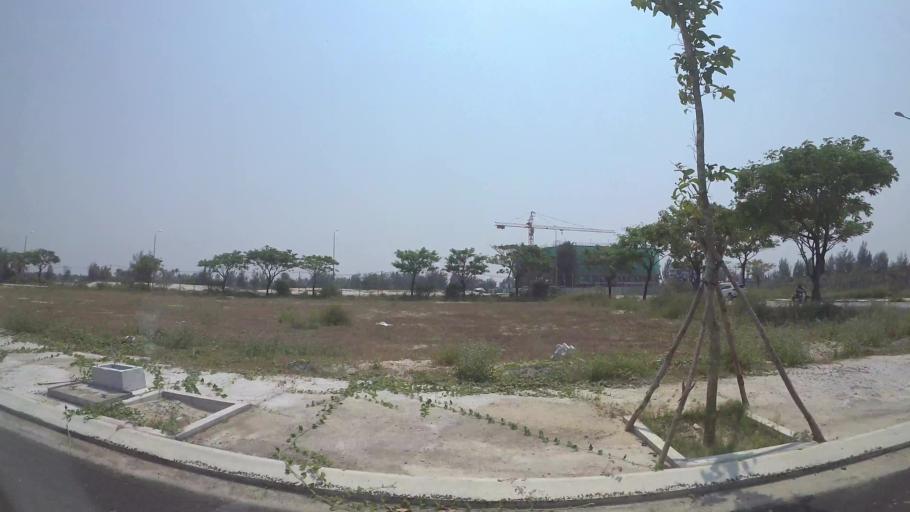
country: VN
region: Da Nang
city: Ngu Hanh Son
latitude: 15.9699
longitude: 108.2612
